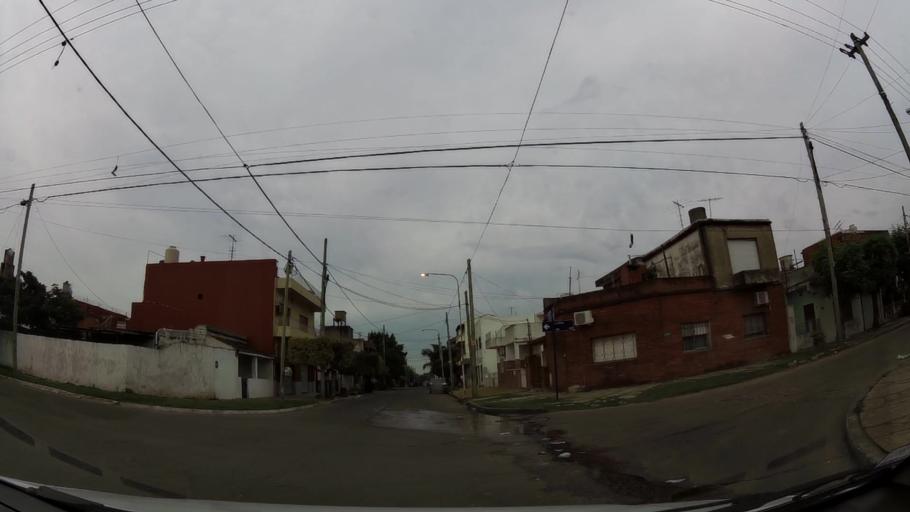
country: AR
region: Buenos Aires F.D.
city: Villa Lugano
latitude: -34.6912
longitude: -58.5139
